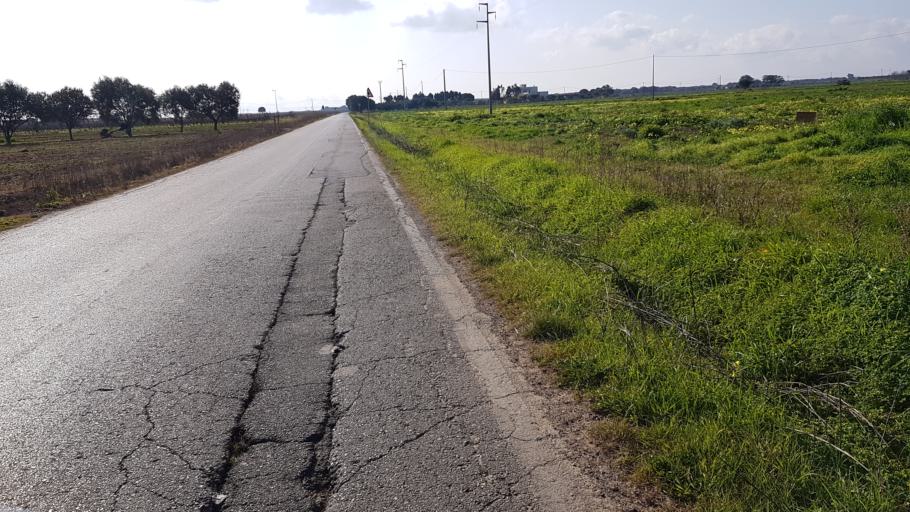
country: IT
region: Apulia
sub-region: Provincia di Brindisi
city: La Rosa
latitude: 40.5831
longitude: 17.9023
